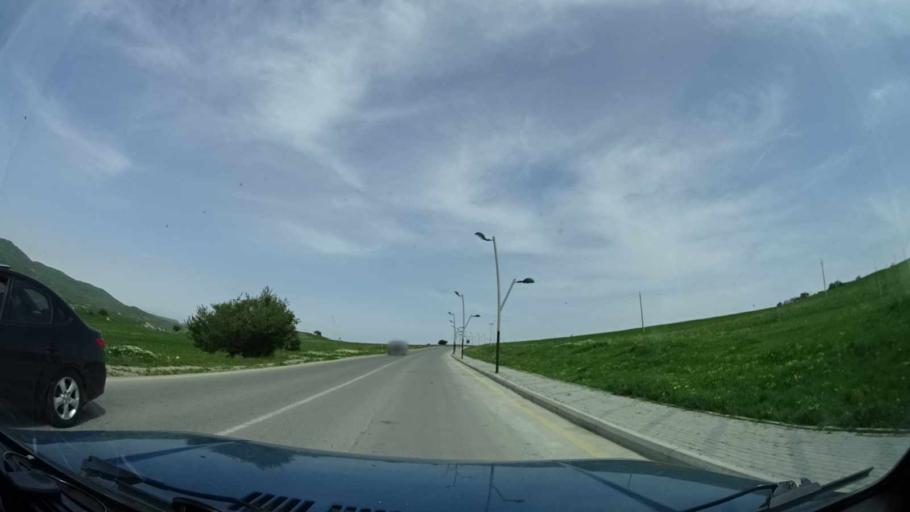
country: AZ
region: Xizi
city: Khyzy
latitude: 40.9099
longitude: 49.0777
